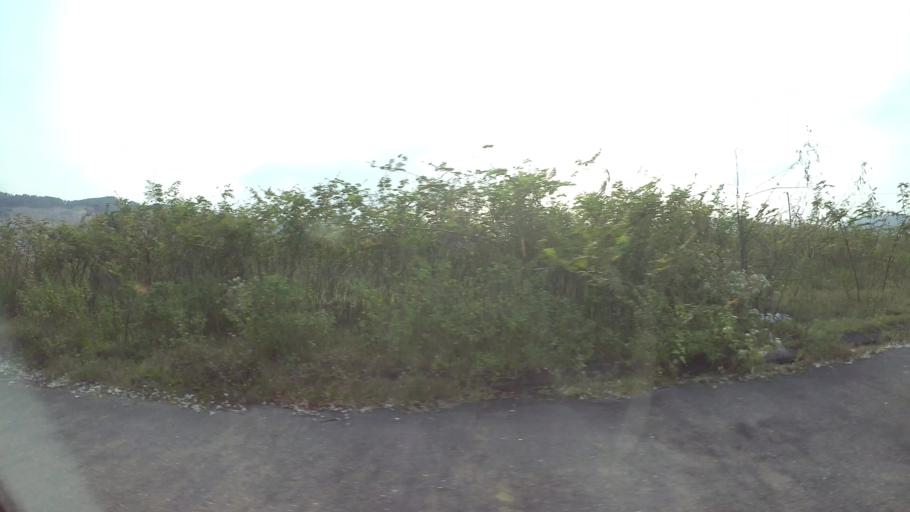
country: VN
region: Da Nang
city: Lien Chieu
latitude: 16.0458
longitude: 108.1582
